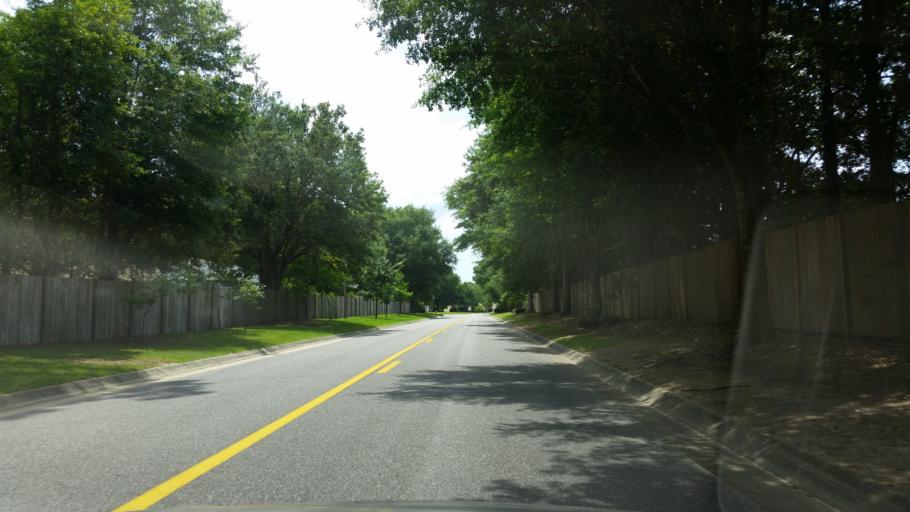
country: US
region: Florida
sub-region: Escambia County
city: Bellview
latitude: 30.4767
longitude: -87.2850
